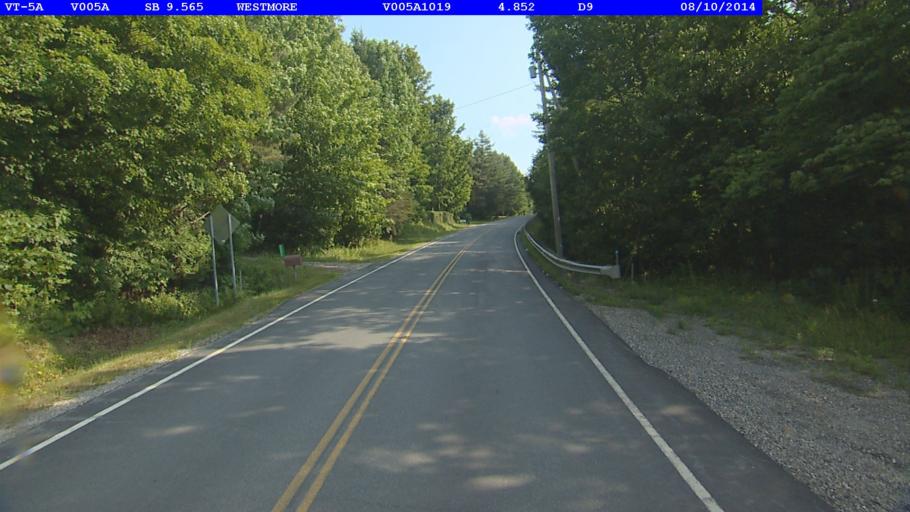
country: US
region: Vermont
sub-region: Caledonia County
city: Lyndonville
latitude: 44.7603
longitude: -72.0523
